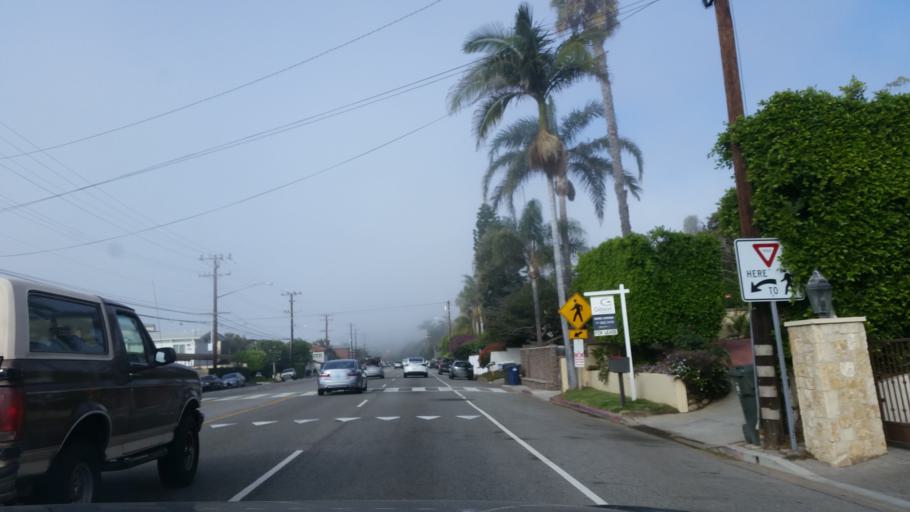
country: US
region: California
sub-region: Los Angeles County
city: Las Flores
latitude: 34.0380
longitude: -118.6413
